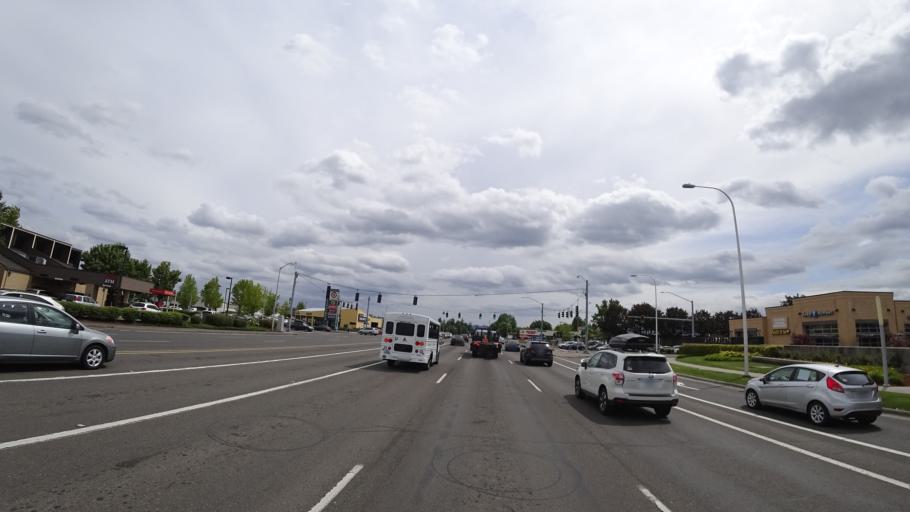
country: US
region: Oregon
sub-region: Washington County
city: Rockcreek
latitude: 45.5388
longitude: -122.8676
